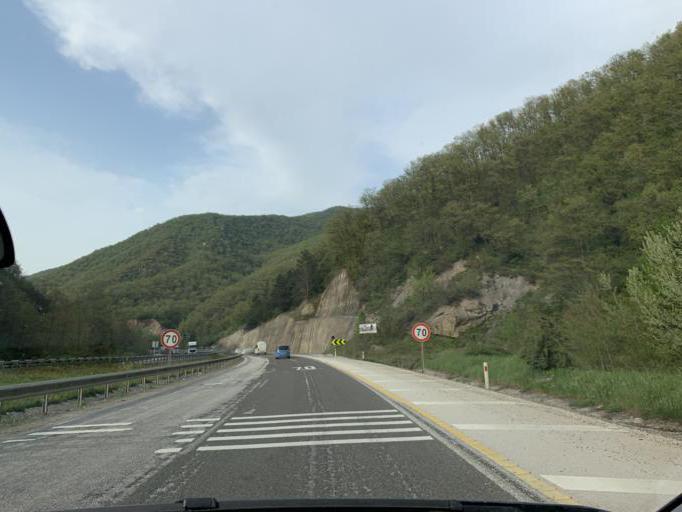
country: TR
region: Bursa
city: Kursunlu
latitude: 39.9942
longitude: 29.6522
